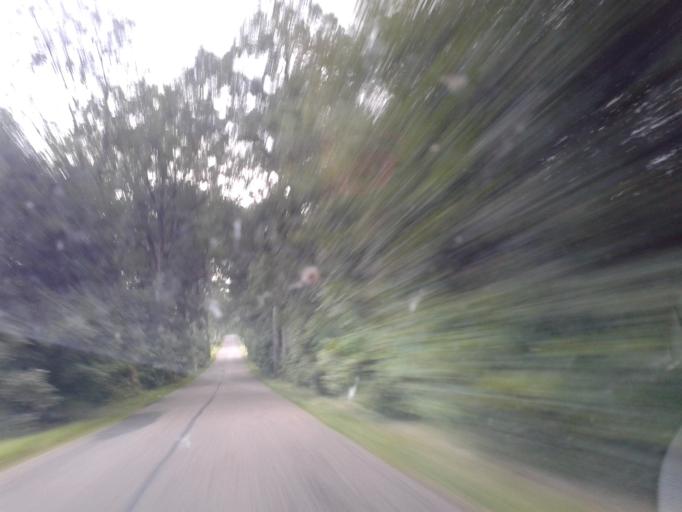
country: PL
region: West Pomeranian Voivodeship
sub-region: Powiat koszalinski
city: Bobolice
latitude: 53.9020
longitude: 16.5349
